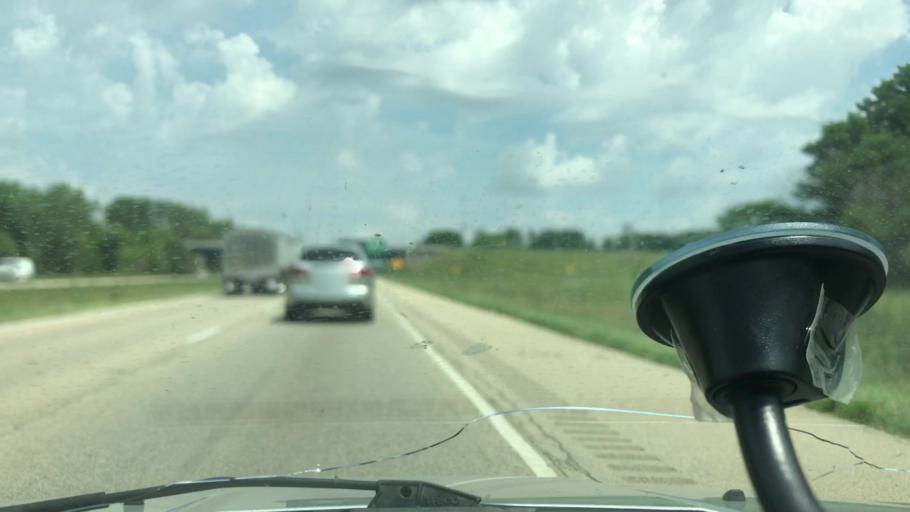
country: US
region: Illinois
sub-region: Peoria County
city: Bellevue
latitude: 40.6916
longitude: -89.6755
